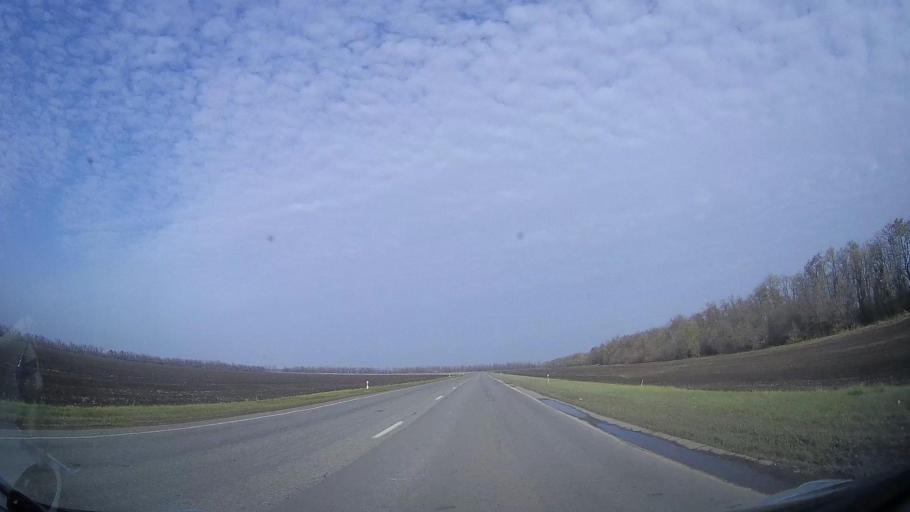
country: RU
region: Rostov
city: Tselina
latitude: 46.5218
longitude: 40.9923
